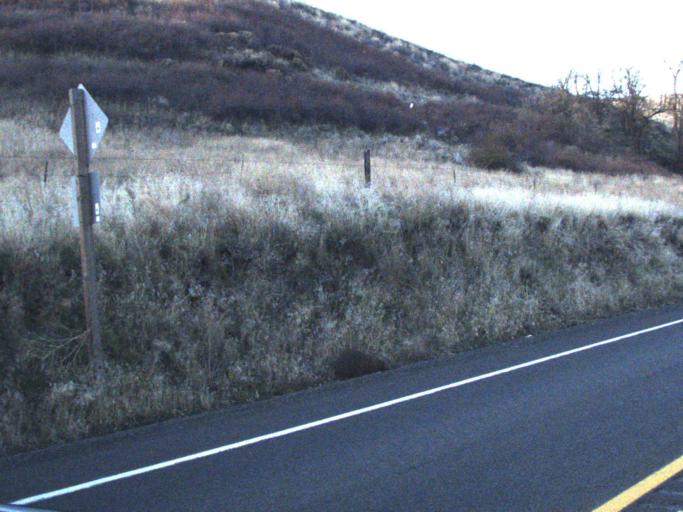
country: US
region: Washington
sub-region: Garfield County
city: Pomeroy
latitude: 46.6723
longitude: -117.8129
